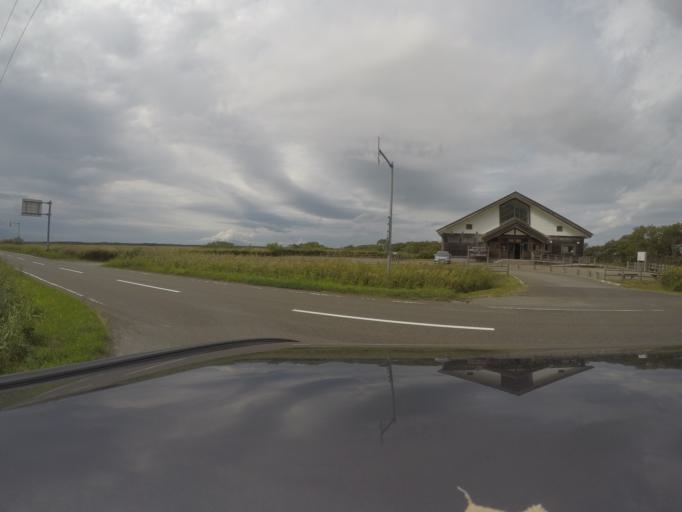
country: JP
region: Hokkaido
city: Makubetsu
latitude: 45.0097
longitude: 141.7310
